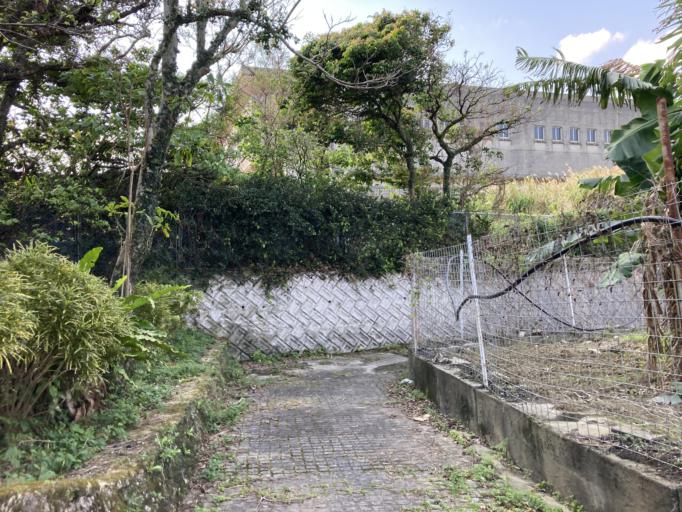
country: JP
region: Okinawa
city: Tomigusuku
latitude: 26.1870
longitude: 127.7246
